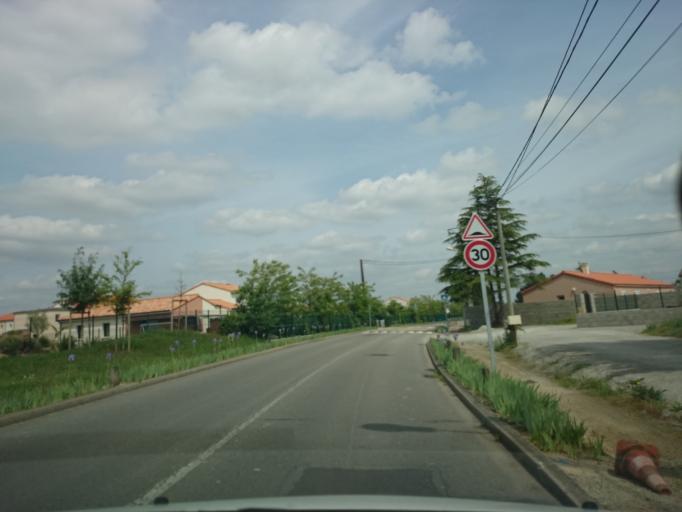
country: FR
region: Pays de la Loire
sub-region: Departement de la Loire-Atlantique
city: Pont-Saint-Martin
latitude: 47.1248
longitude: -1.6126
